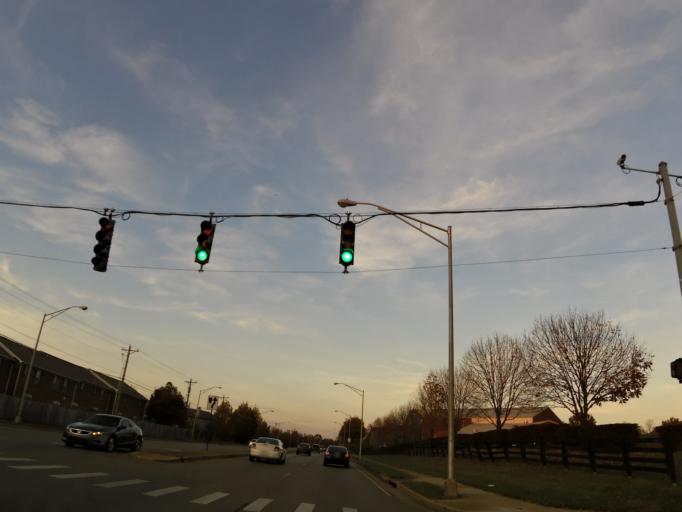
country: US
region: Kentucky
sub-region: Fayette County
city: Lexington
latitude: 37.9669
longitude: -84.4768
